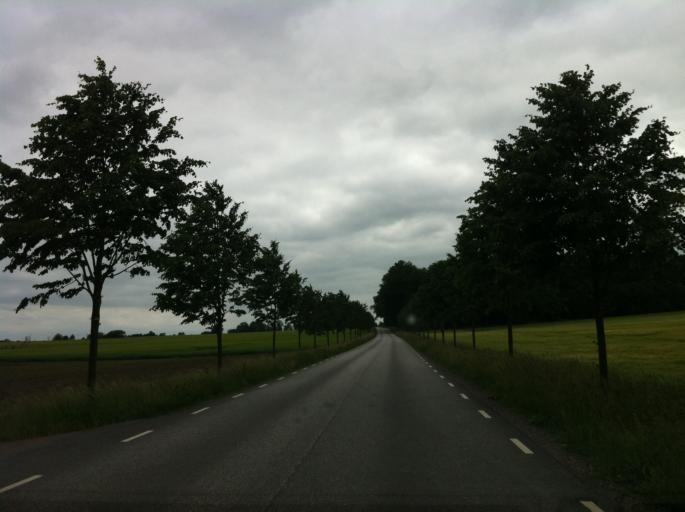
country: SE
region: Skane
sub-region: Hoors Kommun
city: Loberod
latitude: 55.7955
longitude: 13.4223
